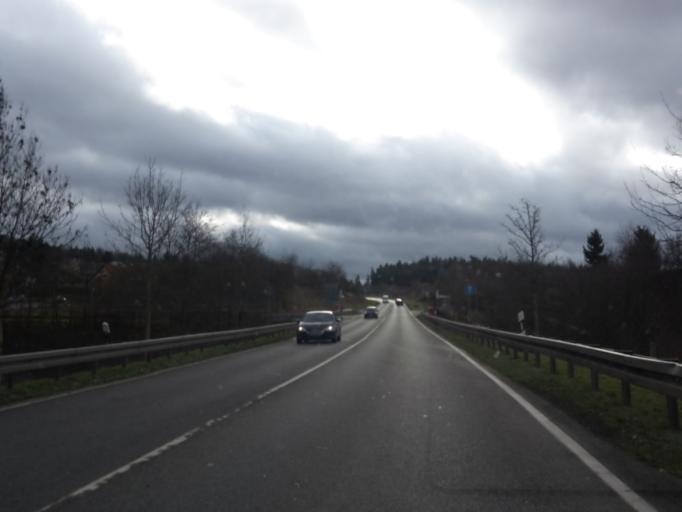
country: DE
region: Hesse
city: Taunusstein
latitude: 50.1581
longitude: 8.2120
